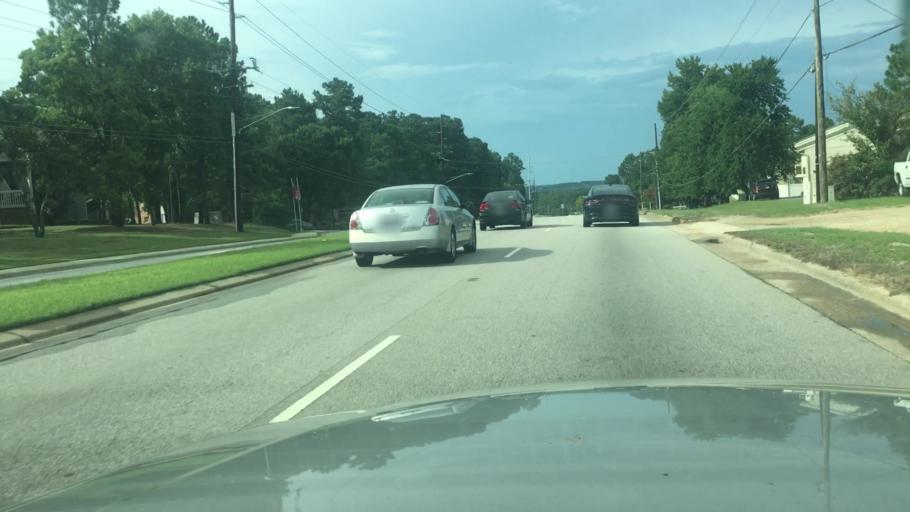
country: US
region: North Carolina
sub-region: Cumberland County
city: Eastover
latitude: 35.1409
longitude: -78.8737
